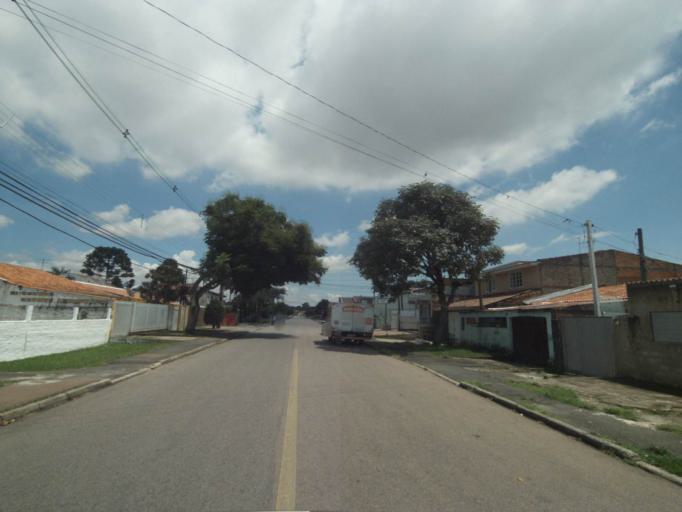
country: BR
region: Parana
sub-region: Pinhais
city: Pinhais
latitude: -25.4764
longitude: -49.1933
